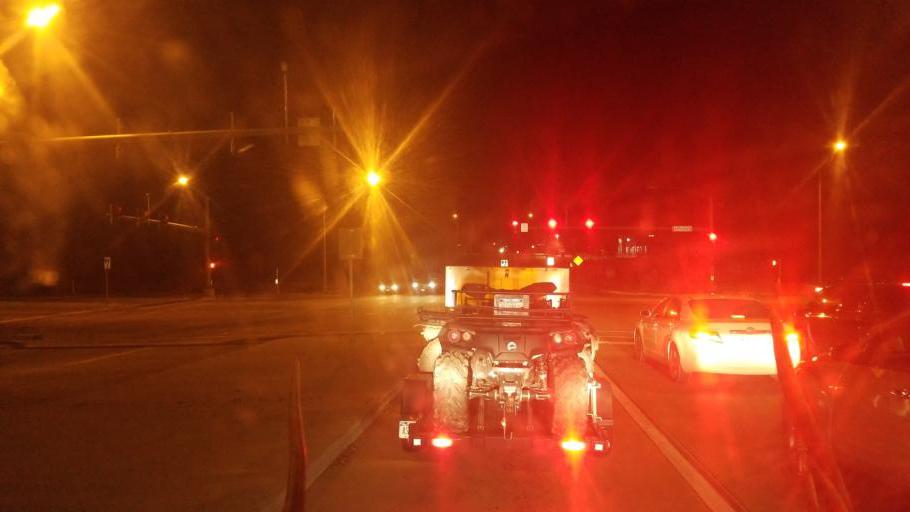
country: US
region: Missouri
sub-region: Jackson County
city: Grain Valley
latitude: 39.0234
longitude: -94.1978
